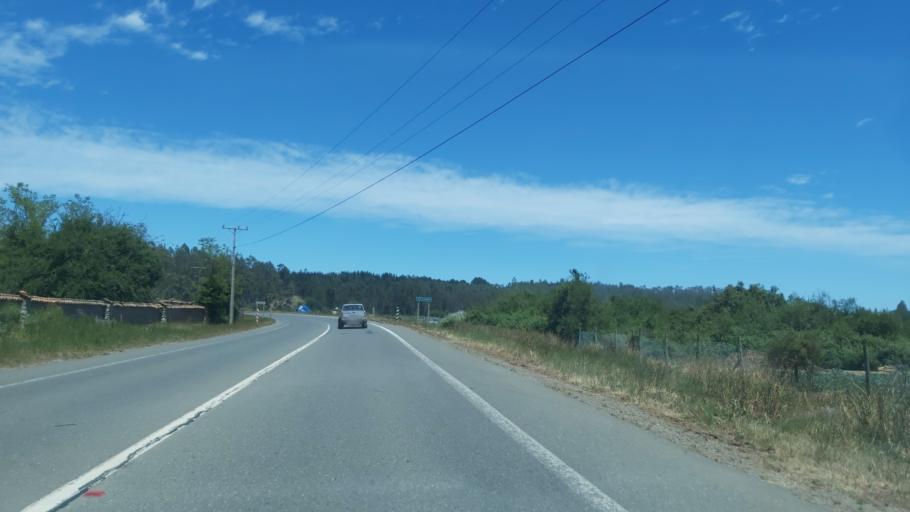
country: CL
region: Maule
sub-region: Provincia de Talca
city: Constitucion
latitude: -35.3126
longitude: -72.3832
